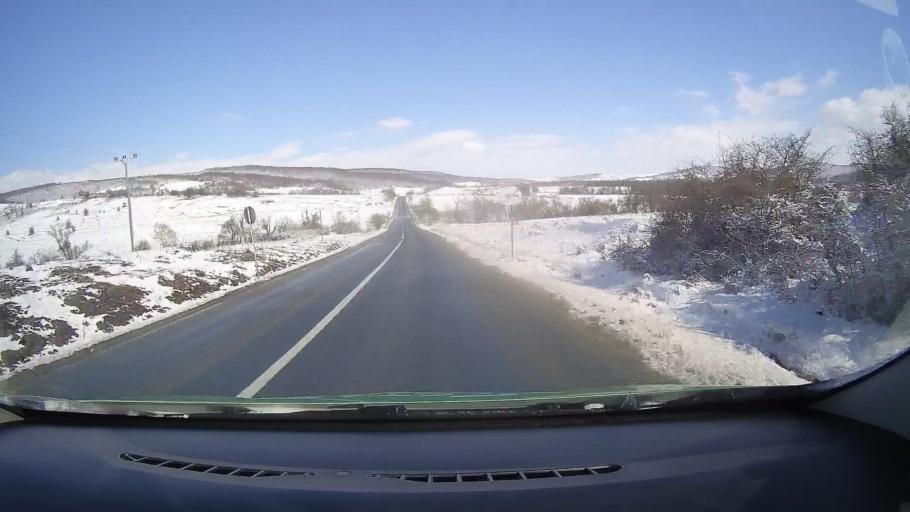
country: RO
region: Sibiu
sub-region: Comuna Rosia
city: Rosia
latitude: 45.8199
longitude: 24.3798
